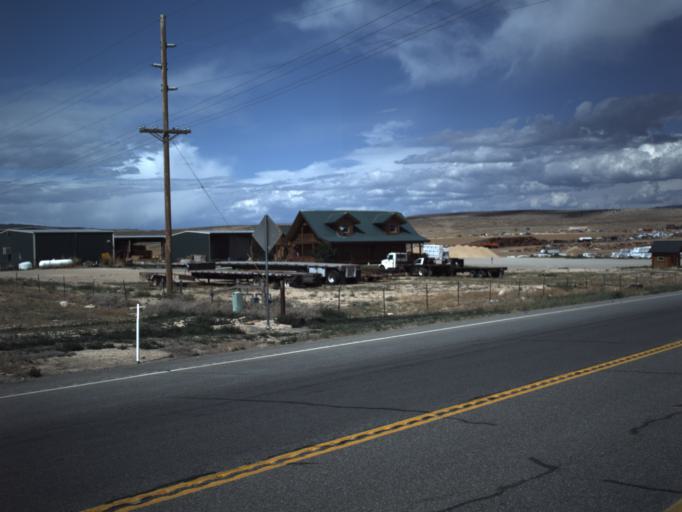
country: US
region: Utah
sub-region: Sanpete County
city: Gunnison
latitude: 39.1602
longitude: -111.7980
